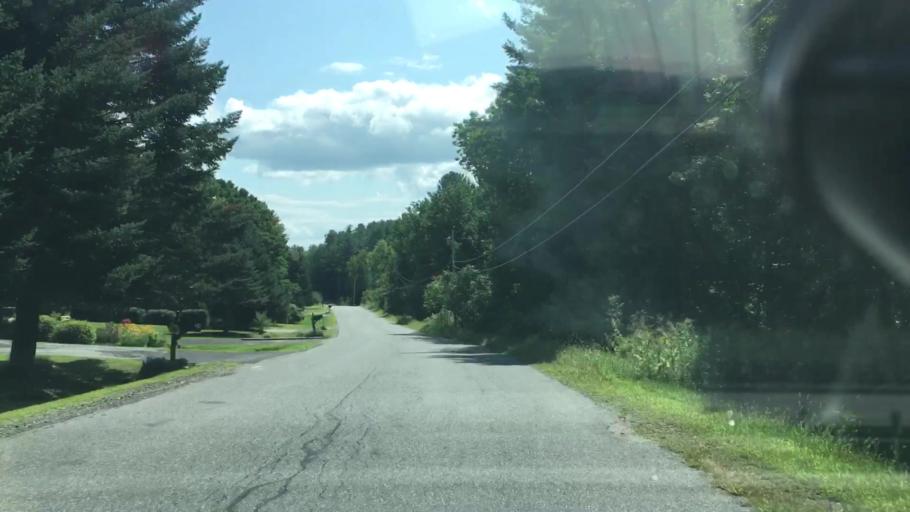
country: US
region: Maine
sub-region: Somerset County
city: Skowhegan
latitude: 44.6773
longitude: -69.6861
